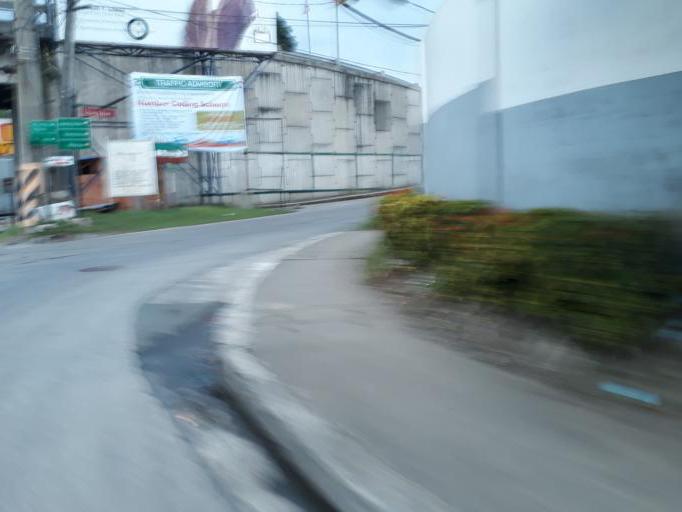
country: PH
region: Central Luzon
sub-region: Province of Bulacan
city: Meycauayan
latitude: 14.7222
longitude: 120.9857
